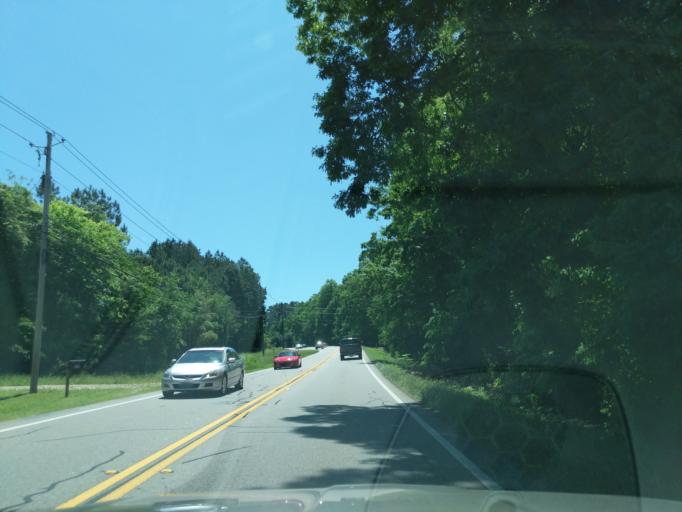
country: US
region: Georgia
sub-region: Columbia County
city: Evans
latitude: 33.5613
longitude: -82.1034
